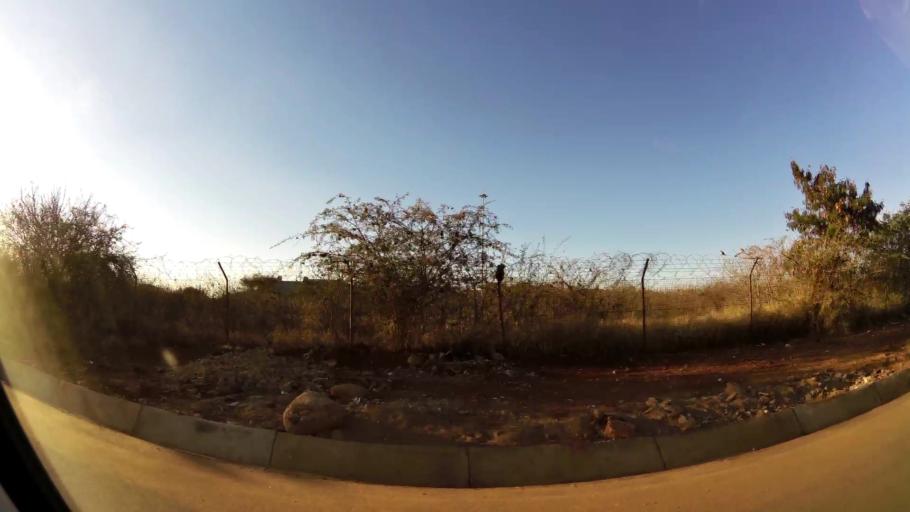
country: ZA
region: Limpopo
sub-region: Waterberg District Municipality
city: Mokopane
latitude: -24.1510
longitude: 28.9929
